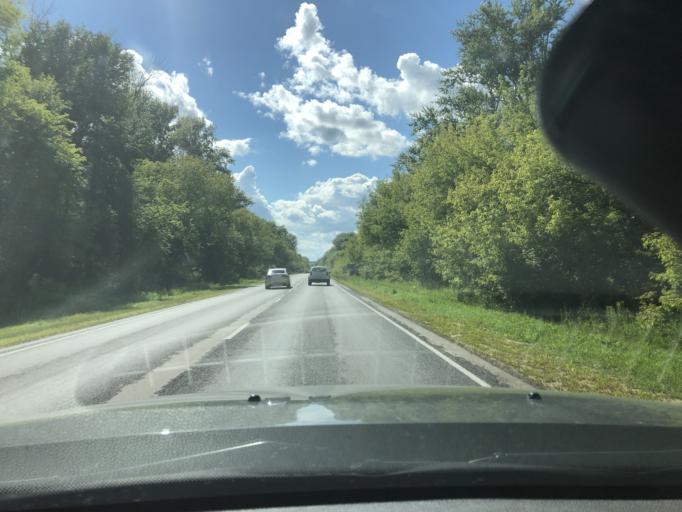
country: RU
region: Tula
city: Kimovsk
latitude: 53.9712
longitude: 38.4841
